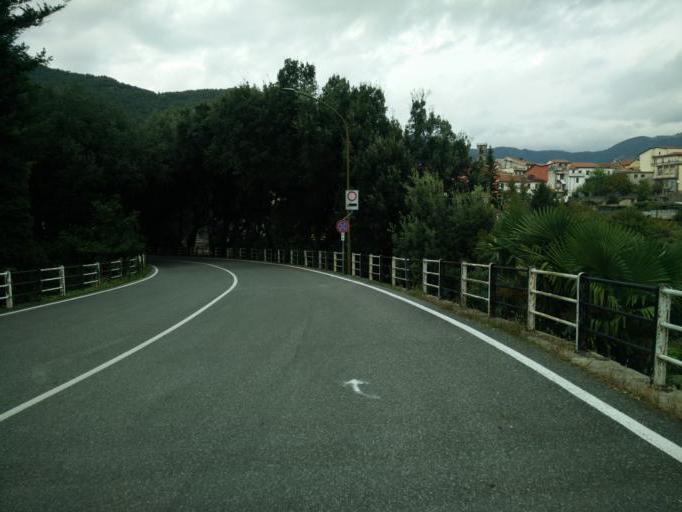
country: IT
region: Tuscany
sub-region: Provincia di Massa-Carrara
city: Fivizzano
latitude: 44.2352
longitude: 10.1229
